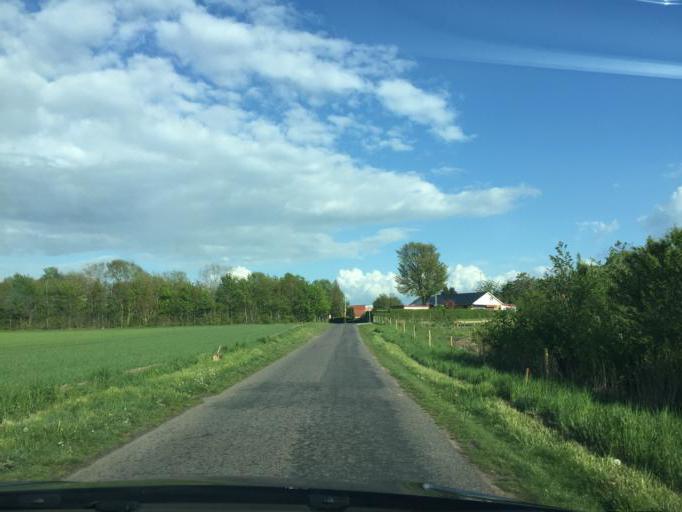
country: DK
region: South Denmark
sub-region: Odense Kommune
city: Bellinge
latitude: 55.3584
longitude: 10.3075
